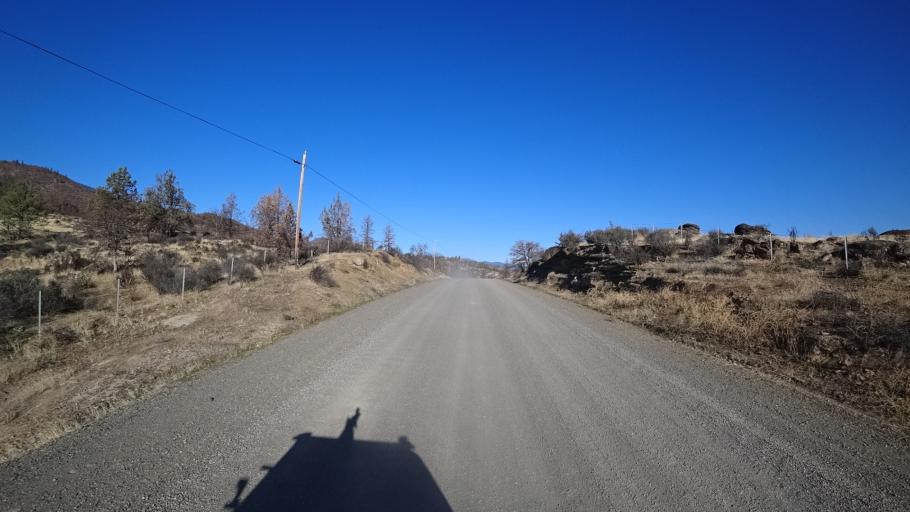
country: US
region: California
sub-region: Siskiyou County
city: Montague
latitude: 41.8957
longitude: -122.5657
